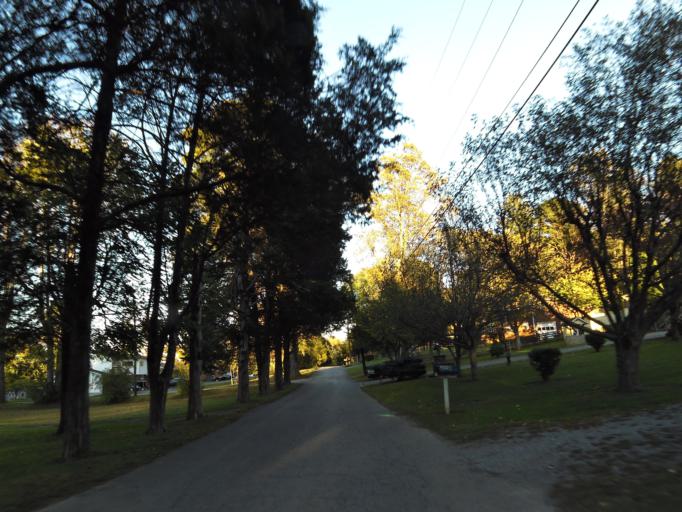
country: US
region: Tennessee
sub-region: Knox County
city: Knoxville
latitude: 36.0159
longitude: -84.0023
